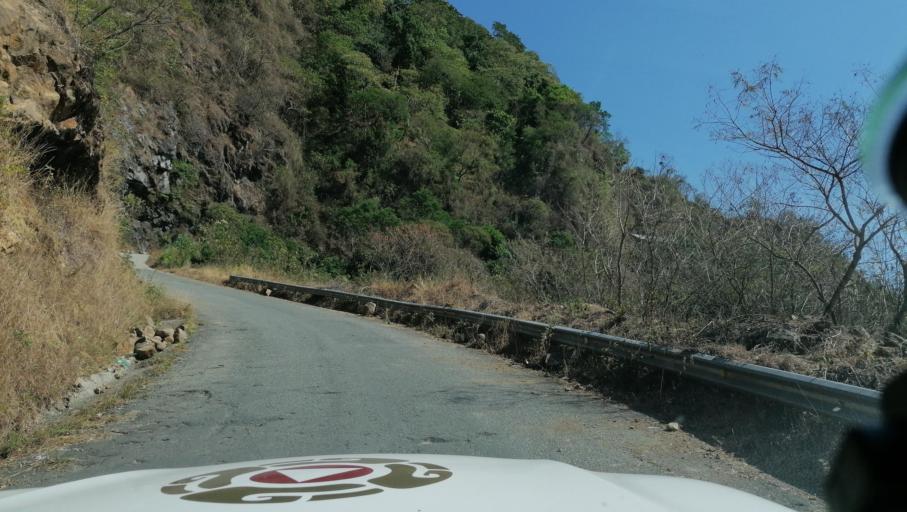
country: MX
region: Chiapas
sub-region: Cacahoatan
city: Benito Juarez
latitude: 15.1845
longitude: -92.1873
